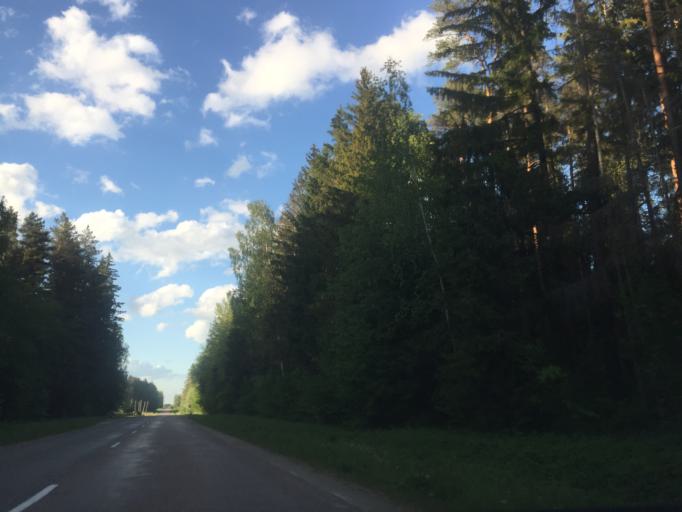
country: LV
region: Kandava
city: Kandava
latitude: 57.0068
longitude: 22.7814
